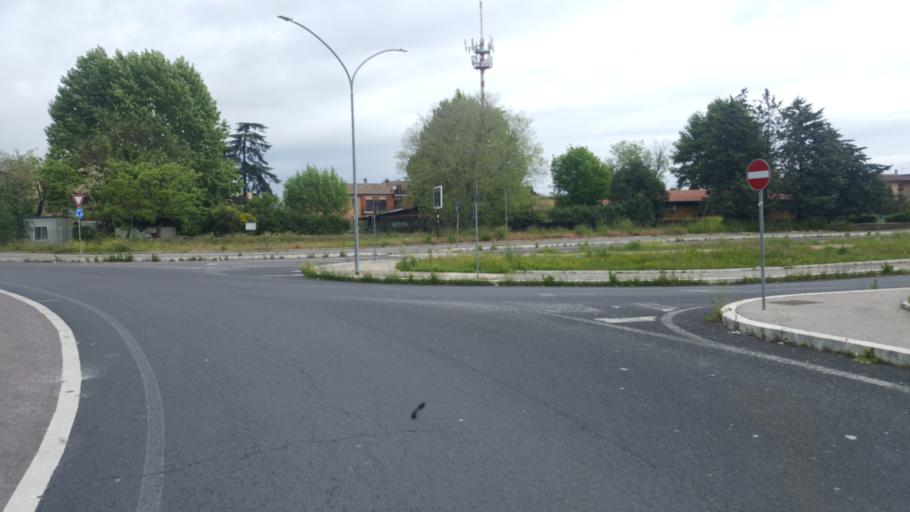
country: IT
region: Latium
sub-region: Citta metropolitana di Roma Capitale
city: Setteville
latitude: 41.9381
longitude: 12.6246
